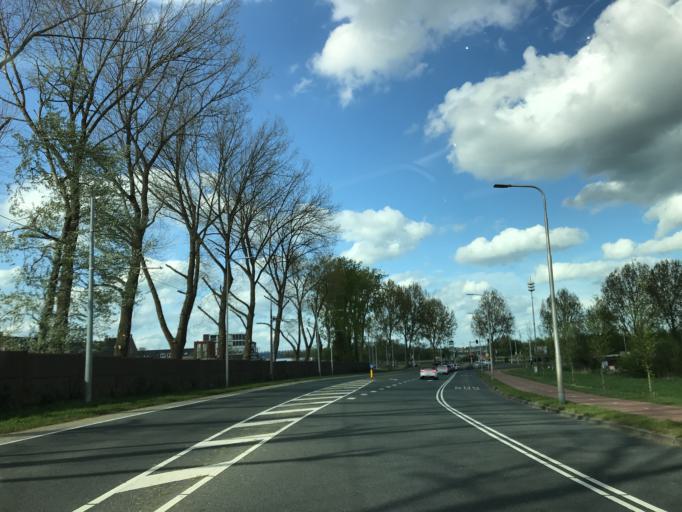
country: NL
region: North Holland
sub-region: Gemeente Diemen
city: Diemen
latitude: 52.3327
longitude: 4.9759
